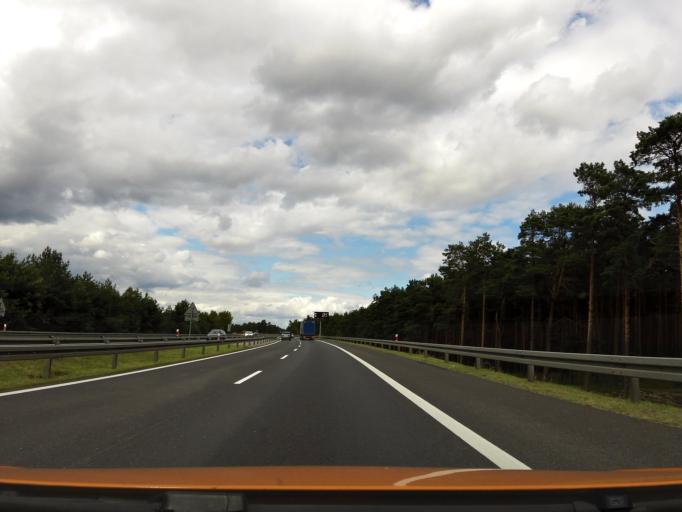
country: PL
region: West Pomeranian Voivodeship
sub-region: Powiat goleniowski
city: Goleniow
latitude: 53.5276
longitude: 14.8112
